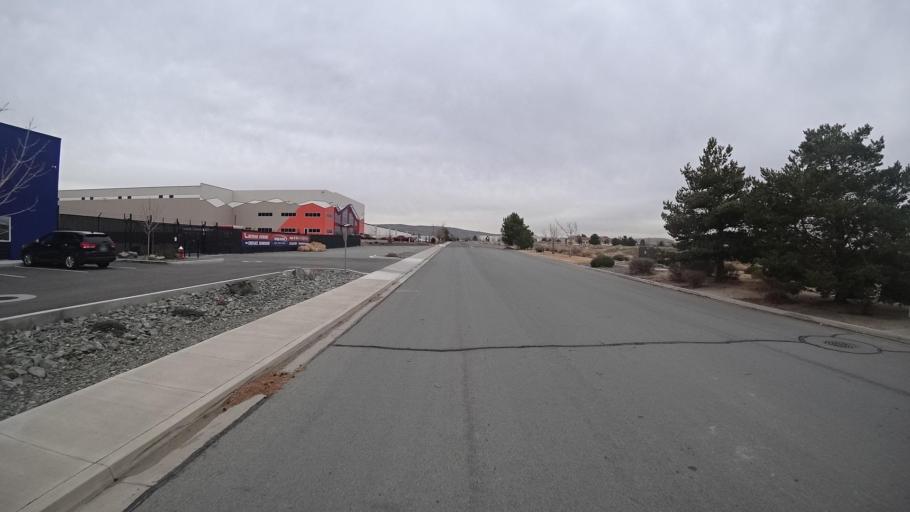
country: US
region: Nevada
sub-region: Washoe County
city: Spanish Springs
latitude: 39.6748
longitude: -119.7088
